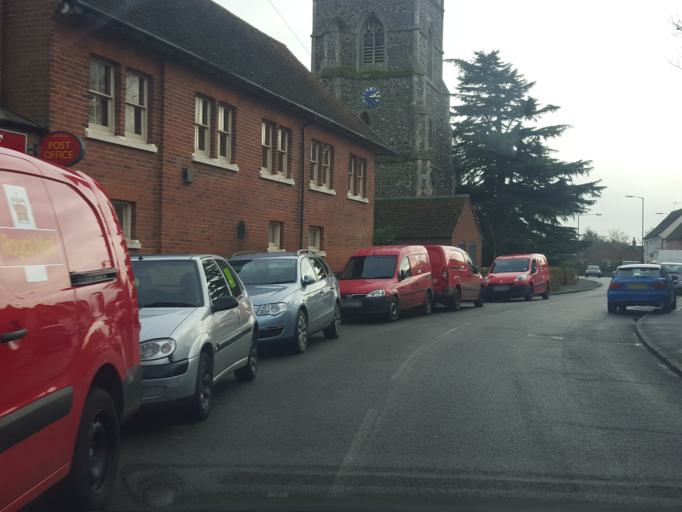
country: GB
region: England
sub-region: Suffolk
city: East Bergholt
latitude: 51.9271
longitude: 0.9854
